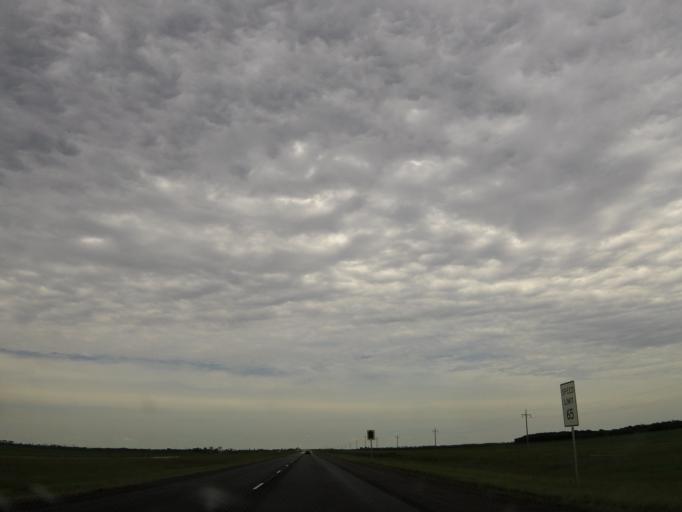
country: US
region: North Dakota
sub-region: Walsh County
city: Grafton
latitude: 48.2458
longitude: -97.1890
